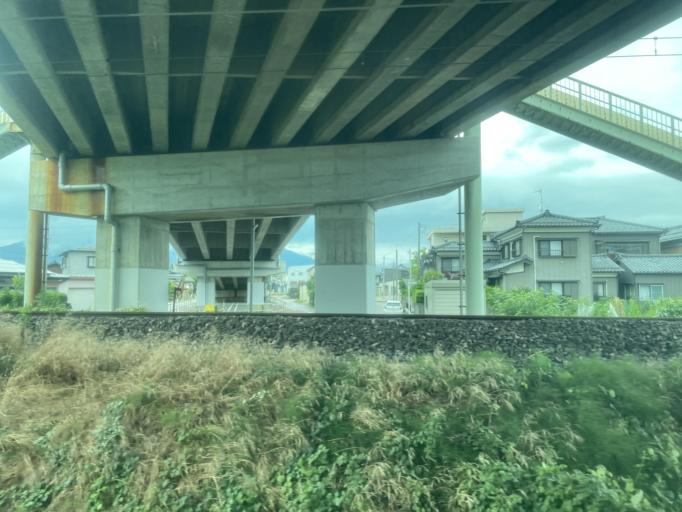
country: JP
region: Niigata
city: Yoshida-kasugacho
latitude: 37.6843
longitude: 138.8740
